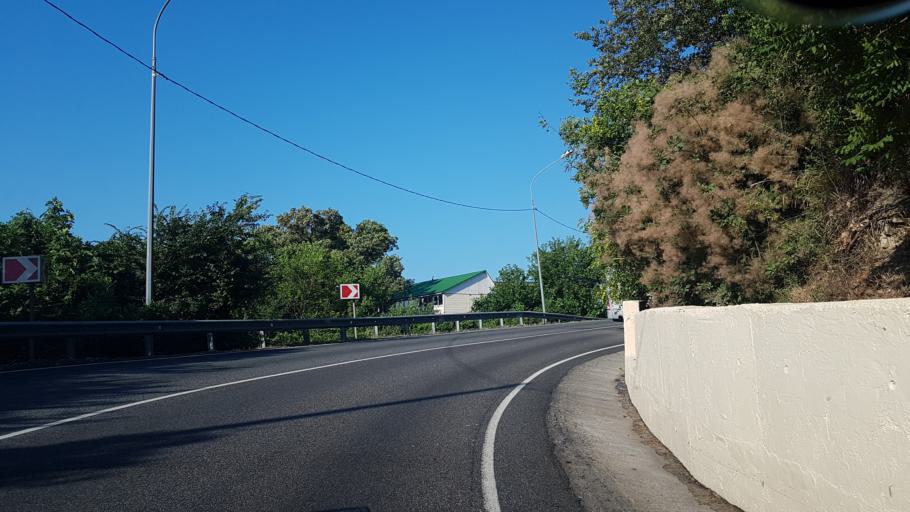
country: RU
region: Krasnodarskiy
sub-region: Sochi City
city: Lazarevskoye
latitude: 43.8519
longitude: 39.4072
